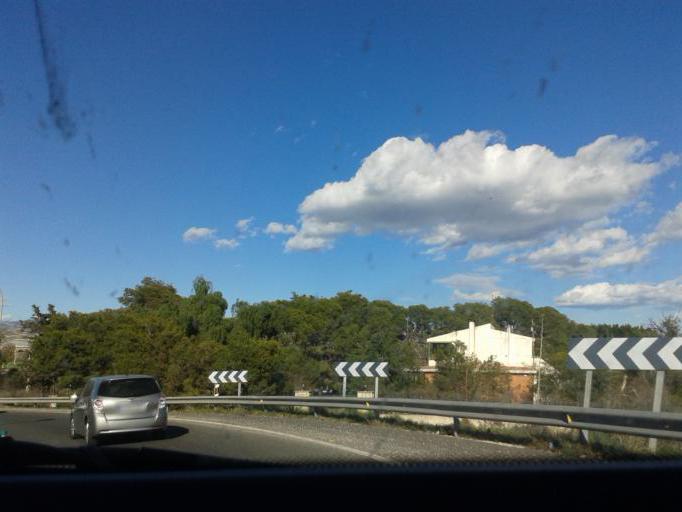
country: ES
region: Valencia
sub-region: Provincia de Alicante
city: San Juan de Alicante
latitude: 38.4136
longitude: -0.4185
